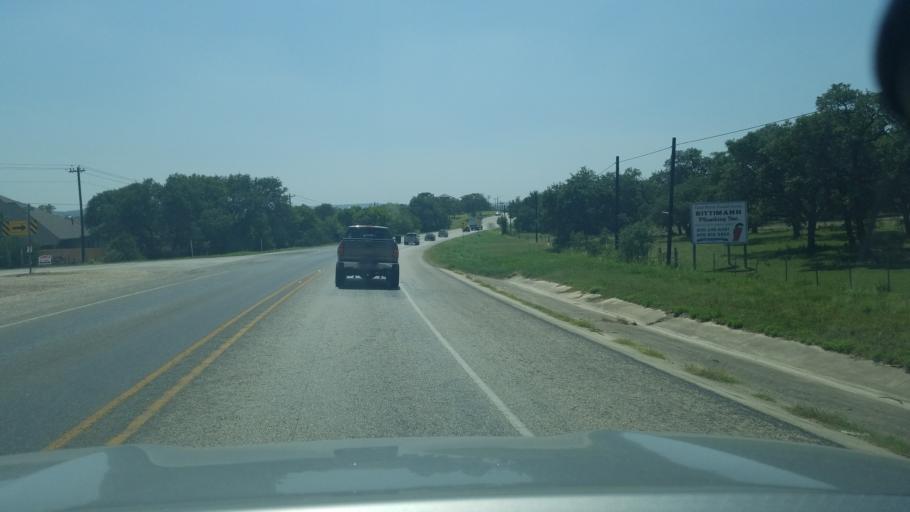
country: US
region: Texas
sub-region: Kendall County
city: Boerne
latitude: 29.7875
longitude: -98.6888
